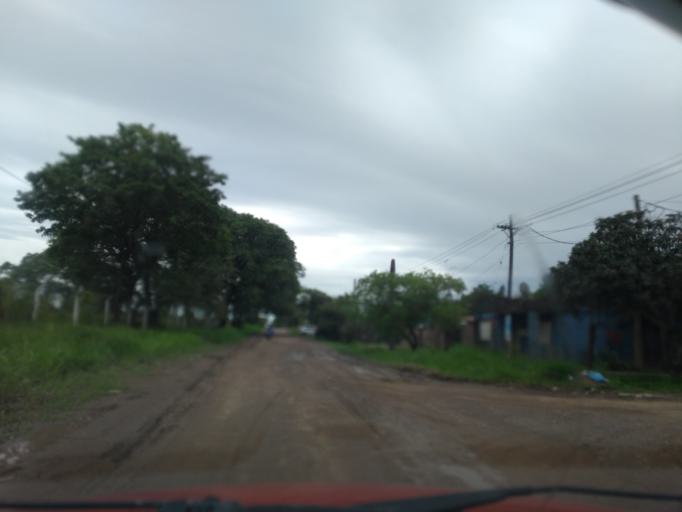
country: AR
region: Chaco
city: Barranqueras
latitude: -27.4797
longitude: -58.9612
